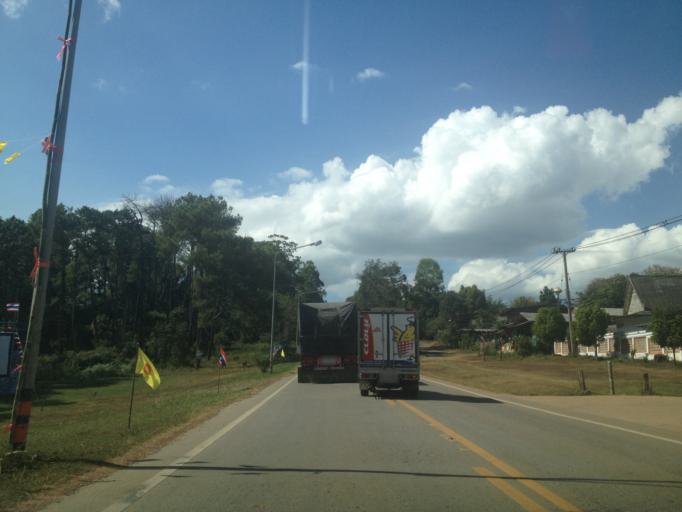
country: TH
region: Chiang Mai
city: Hot
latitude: 18.1466
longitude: 98.3526
